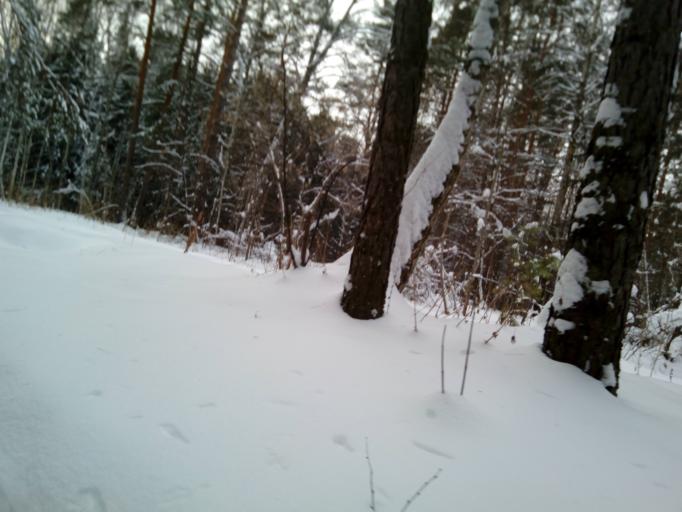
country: RU
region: Novosibirsk
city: Akademgorodok
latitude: 54.8569
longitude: 83.0929
